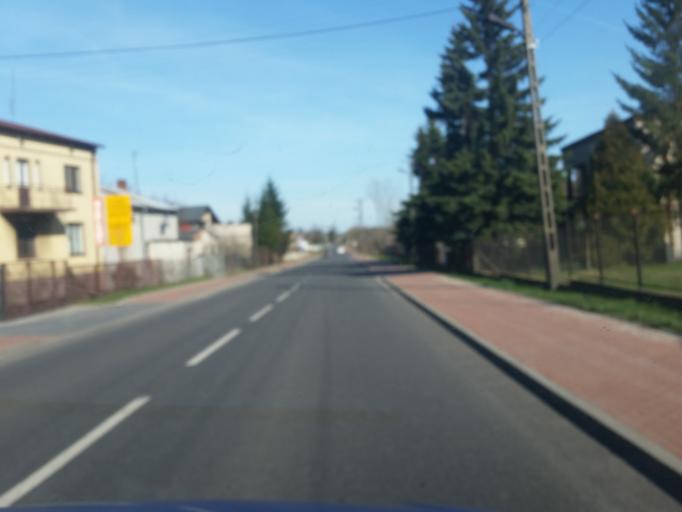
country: PL
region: Lodz Voivodeship
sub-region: Powiat radomszczanski
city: Kamiensk
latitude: 51.2031
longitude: 19.5043
